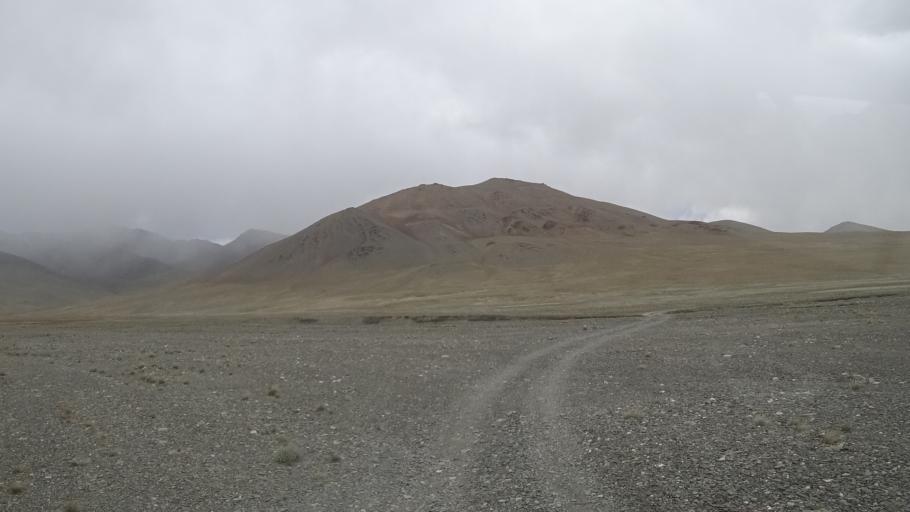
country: TJ
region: Gorno-Badakhshan
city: Murghob
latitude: 37.4917
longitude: 74.0312
